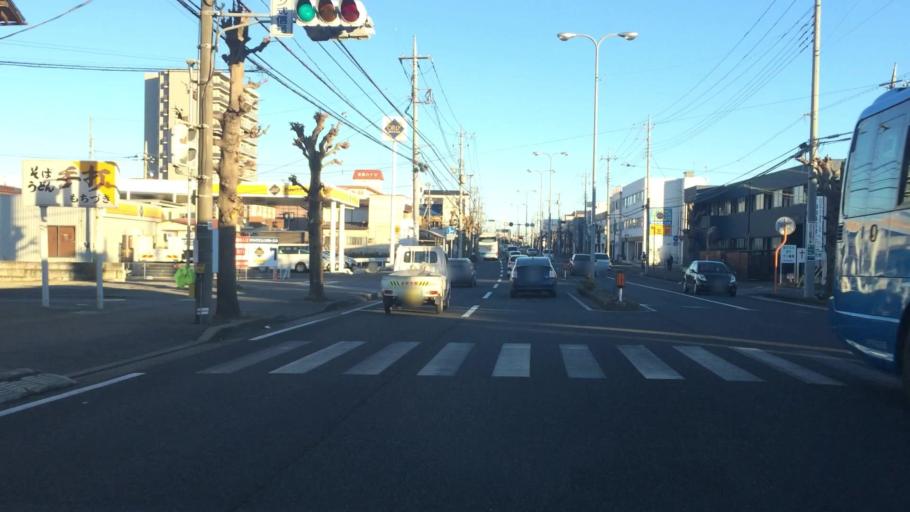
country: JP
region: Tochigi
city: Utsunomiya-shi
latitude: 36.5489
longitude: 139.9241
